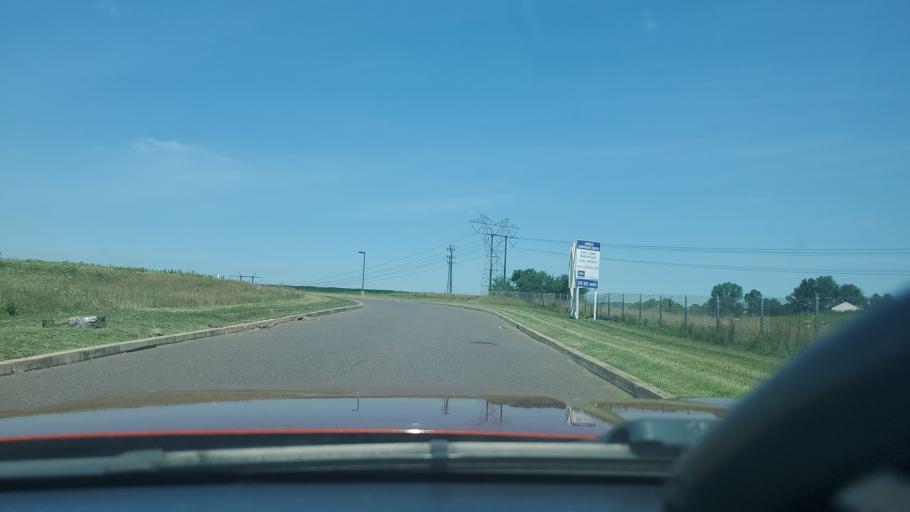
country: US
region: Pennsylvania
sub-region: Montgomery County
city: Limerick
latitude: 40.2221
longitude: -75.5481
